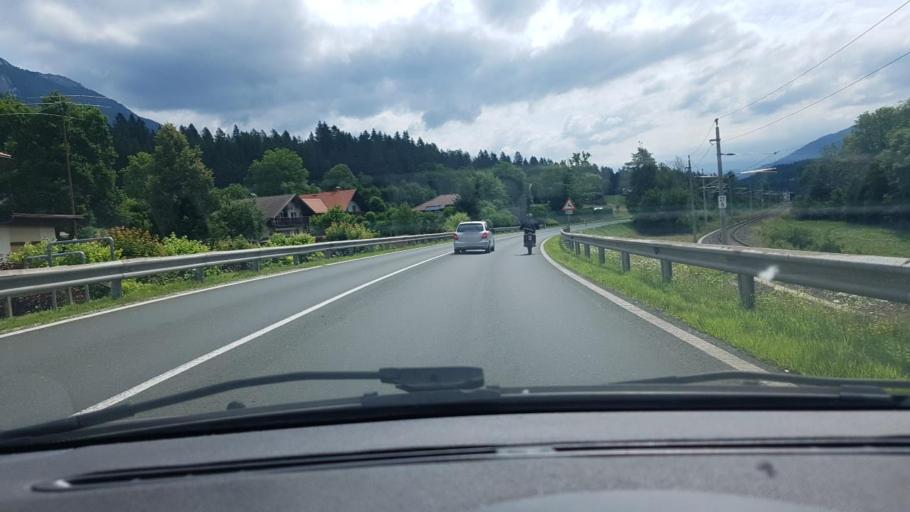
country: AT
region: Carinthia
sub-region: Politischer Bezirk Hermagor
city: Hermagor
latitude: 46.6314
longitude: 13.4111
